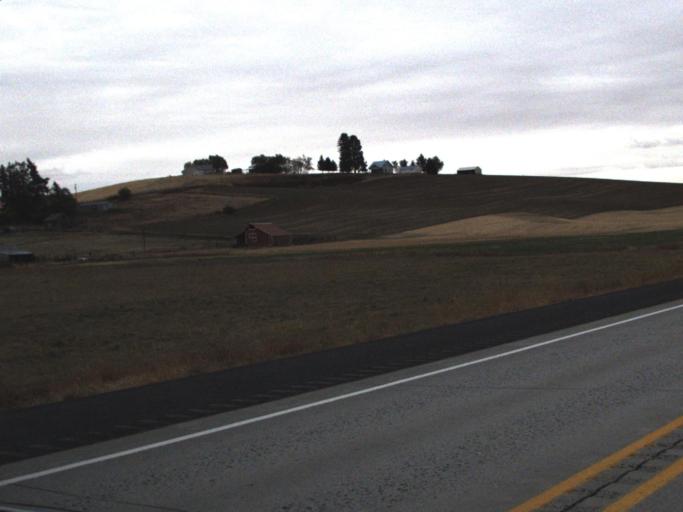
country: US
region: Washington
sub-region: Whitman County
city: Colfax
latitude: 47.0025
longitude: -117.3540
